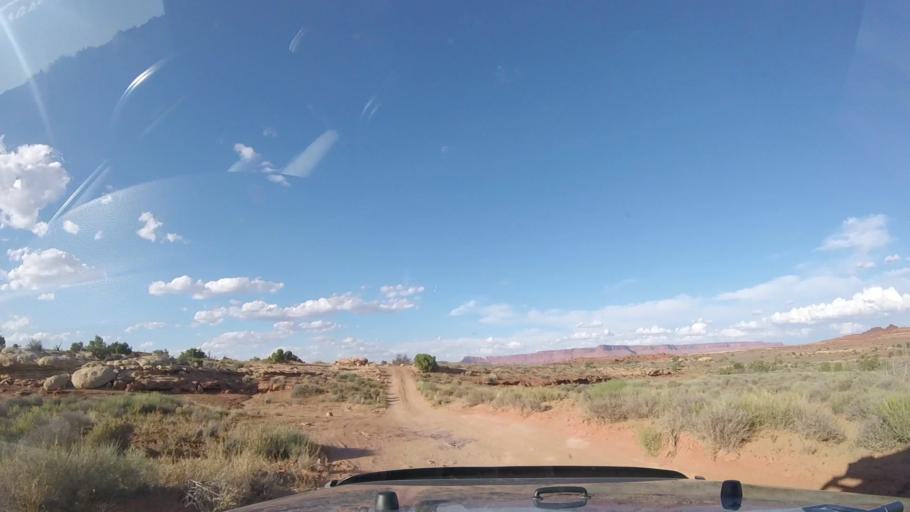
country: US
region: Utah
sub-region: Grand County
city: Moab
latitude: 38.2141
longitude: -109.8028
